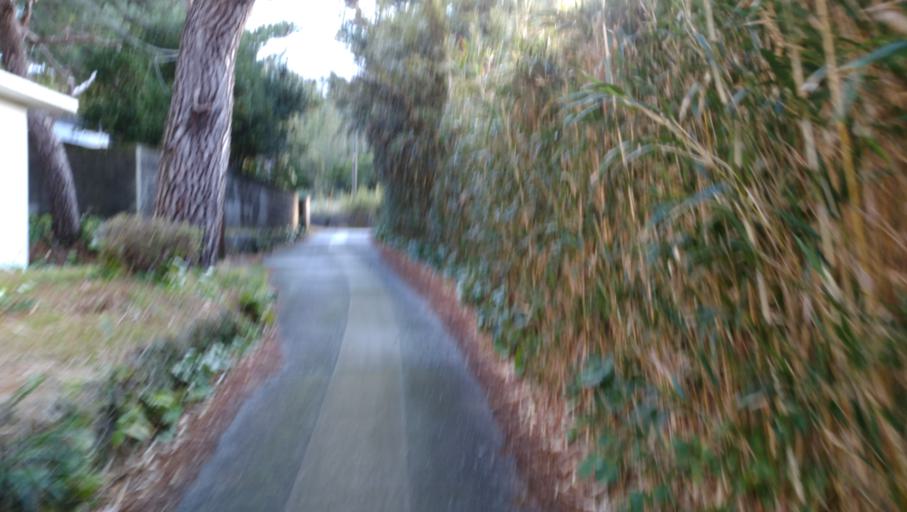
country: JP
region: Kagoshima
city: Makurazaki
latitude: 30.7830
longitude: 130.2797
